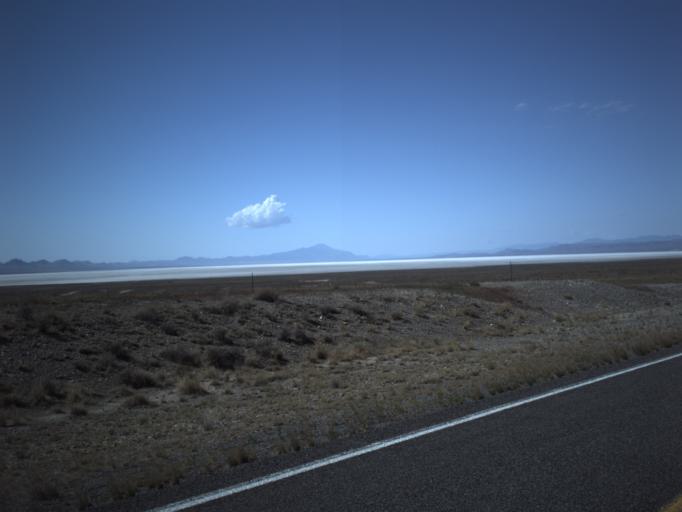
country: US
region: Utah
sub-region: Millard County
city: Delta
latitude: 39.1499
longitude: -113.0698
